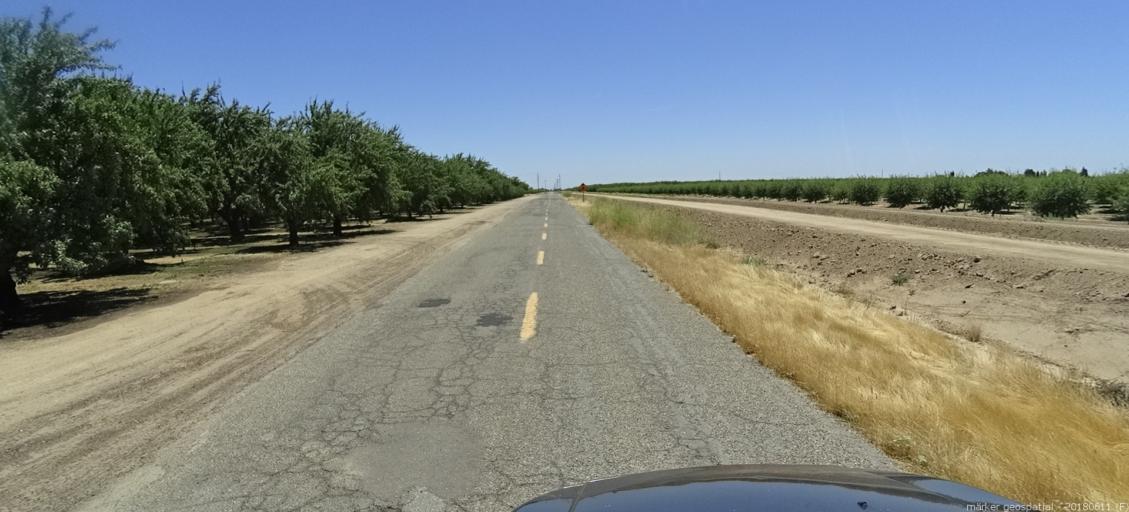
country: US
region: California
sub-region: Madera County
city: Fairmead
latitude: 37.0429
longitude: -120.2114
